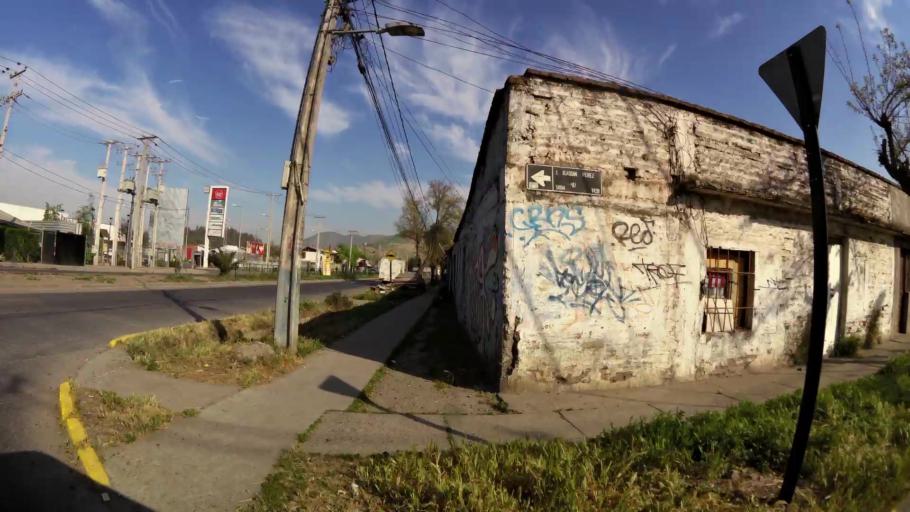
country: CL
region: Santiago Metropolitan
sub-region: Provincia de Maipo
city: San Bernardo
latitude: -33.6079
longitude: -70.7049
